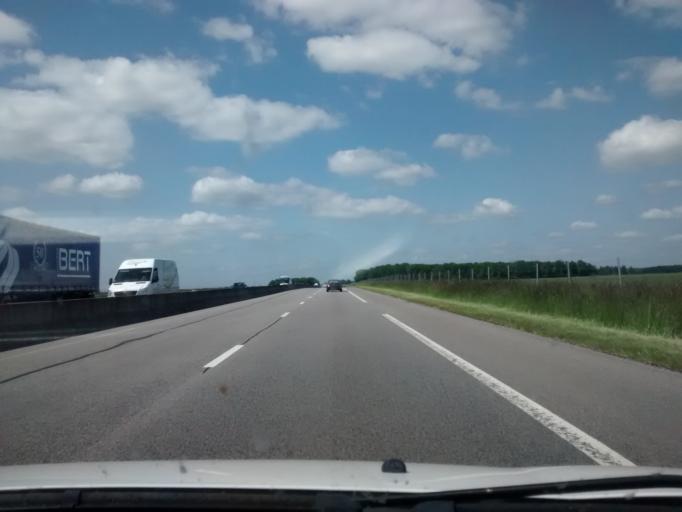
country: FR
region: Ile-de-France
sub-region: Departement des Yvelines
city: Sonchamp
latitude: 48.5970
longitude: 1.8320
